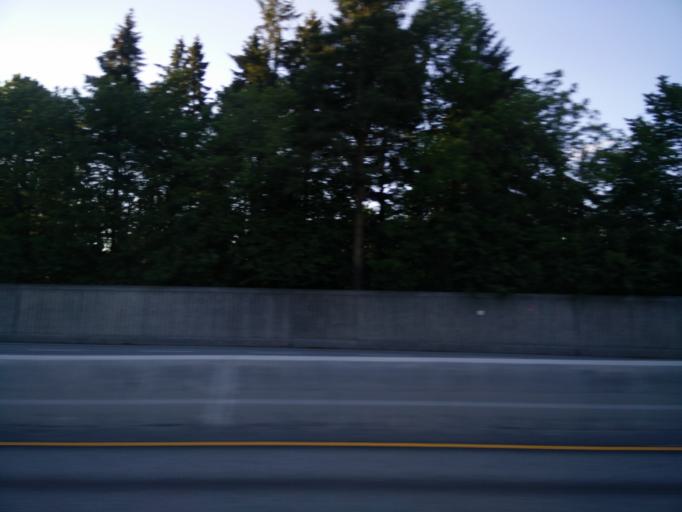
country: NO
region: Akershus
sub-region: Baerum
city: Sandvika
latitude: 59.8946
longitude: 10.5499
